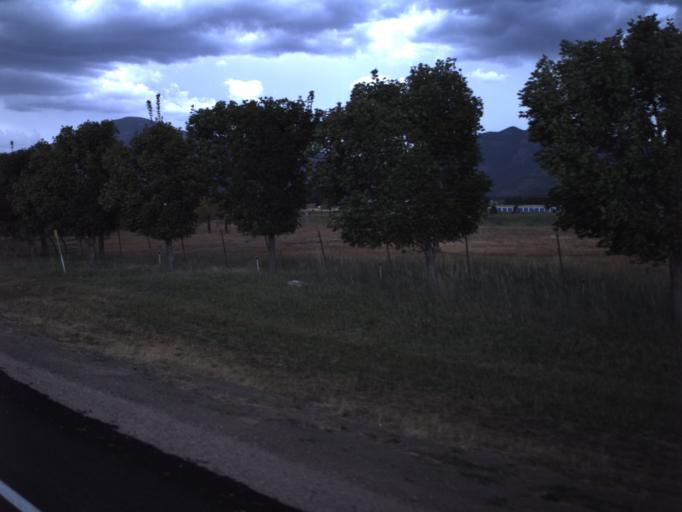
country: US
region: Utah
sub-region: Millard County
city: Fillmore
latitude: 38.9566
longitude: -112.3362
